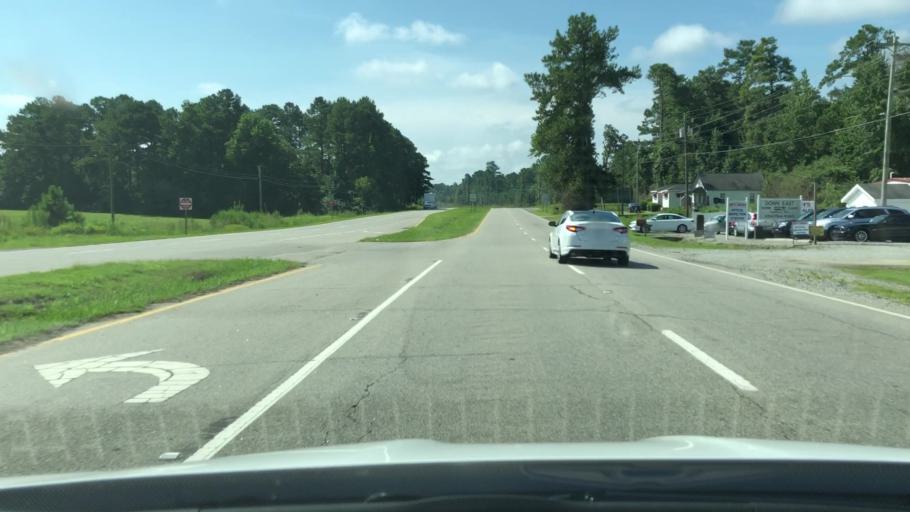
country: US
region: North Carolina
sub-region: Bertie County
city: Windsor
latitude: 35.9767
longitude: -76.9563
